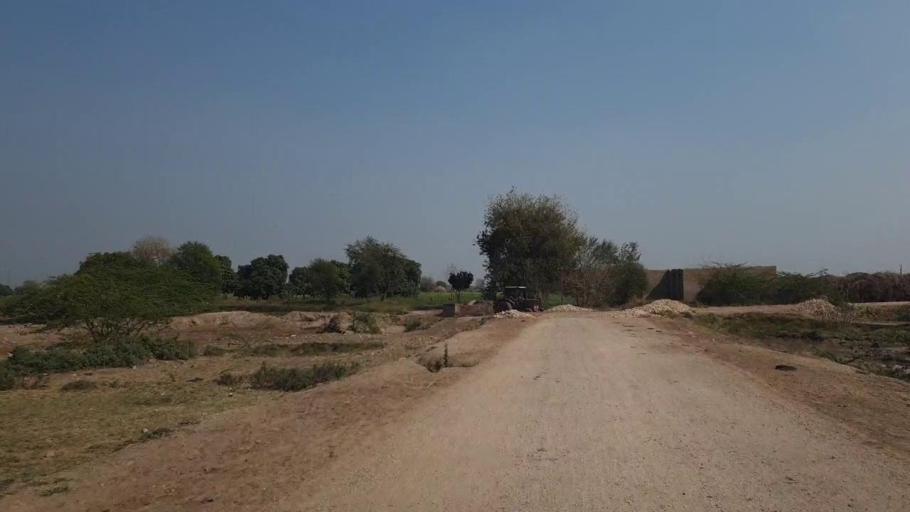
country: PK
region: Sindh
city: Chambar
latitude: 25.3521
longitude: 68.8990
